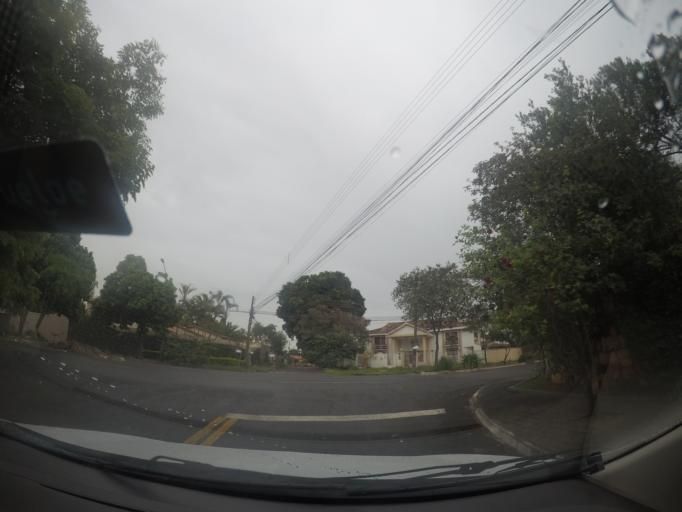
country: BR
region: Goias
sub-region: Goiania
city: Goiania
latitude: -16.6502
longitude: -49.2305
